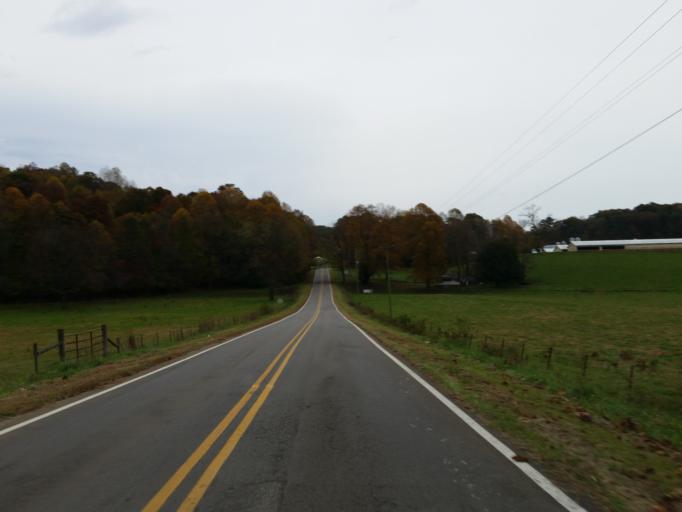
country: US
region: Georgia
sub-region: Gilmer County
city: Ellijay
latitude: 34.6446
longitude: -84.3306
